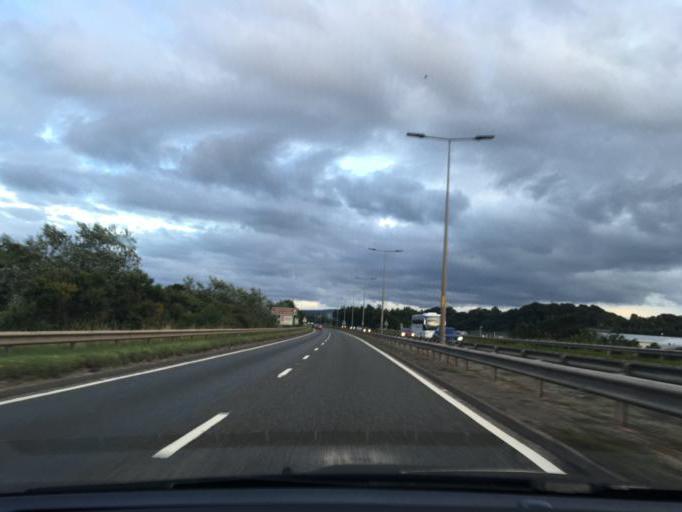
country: GB
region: Scotland
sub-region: Highland
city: Inverness
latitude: 57.4862
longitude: -4.2048
